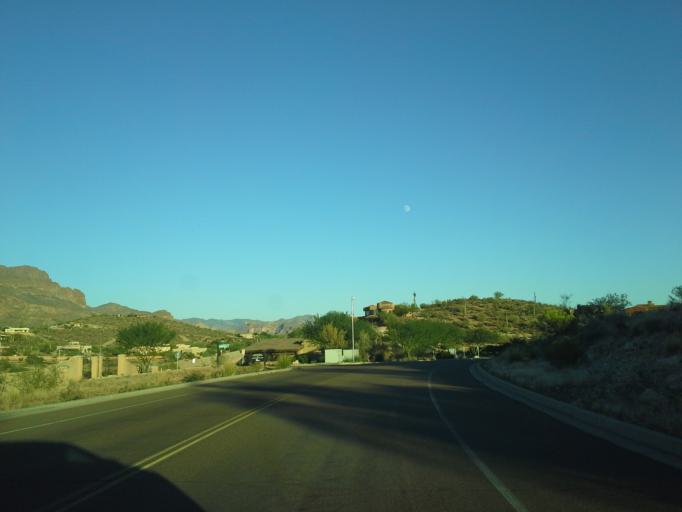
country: US
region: Arizona
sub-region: Pinal County
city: Apache Junction
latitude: 33.3822
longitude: -111.4471
